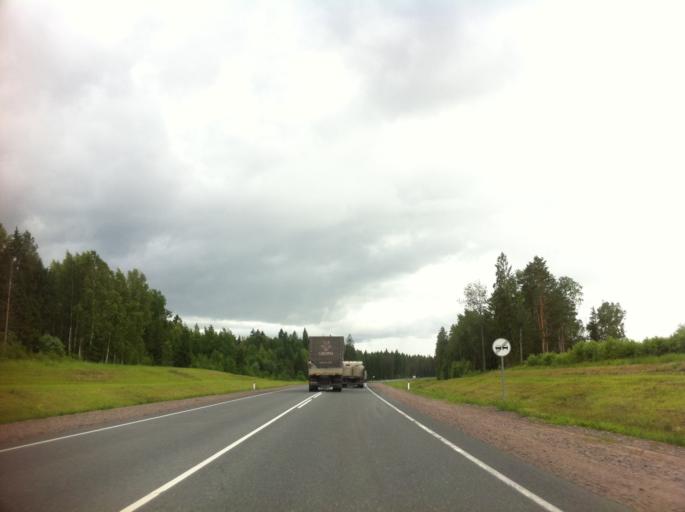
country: RU
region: Leningrad
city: Luga
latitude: 58.6491
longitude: 29.8575
